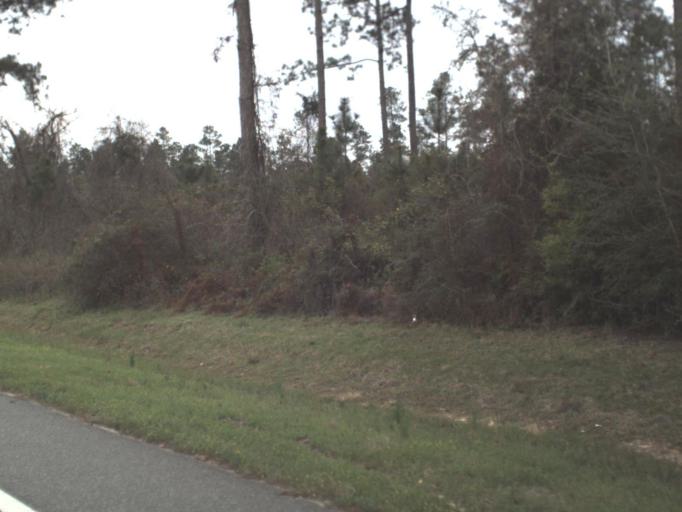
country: US
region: Florida
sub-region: Gulf County
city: Wewahitchka
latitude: 30.2566
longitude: -85.2336
